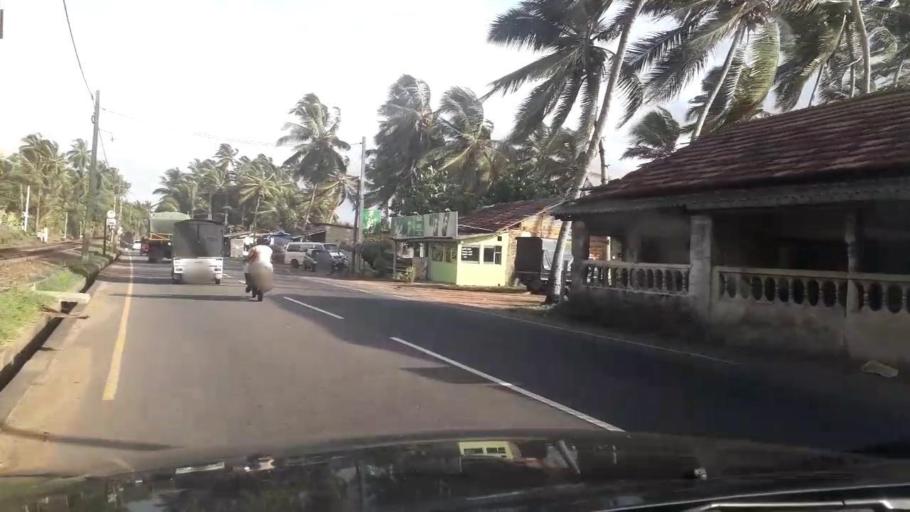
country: LK
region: Western
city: Beruwala
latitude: 6.4969
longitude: 79.9811
